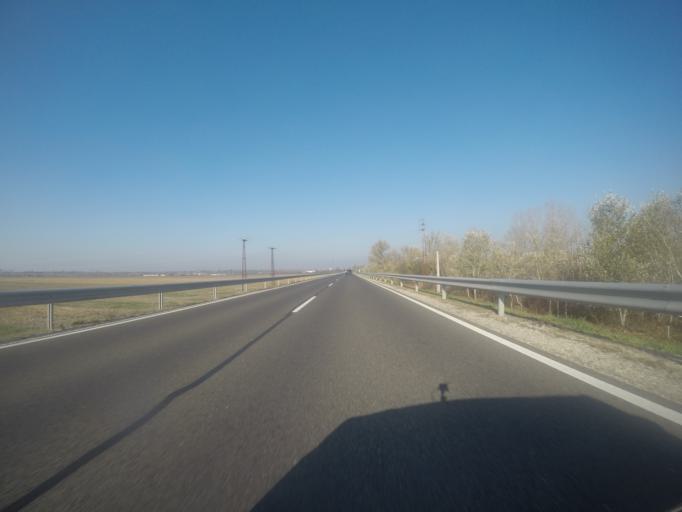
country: HU
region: Fejer
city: Ercsi
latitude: 47.2215
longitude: 18.8887
